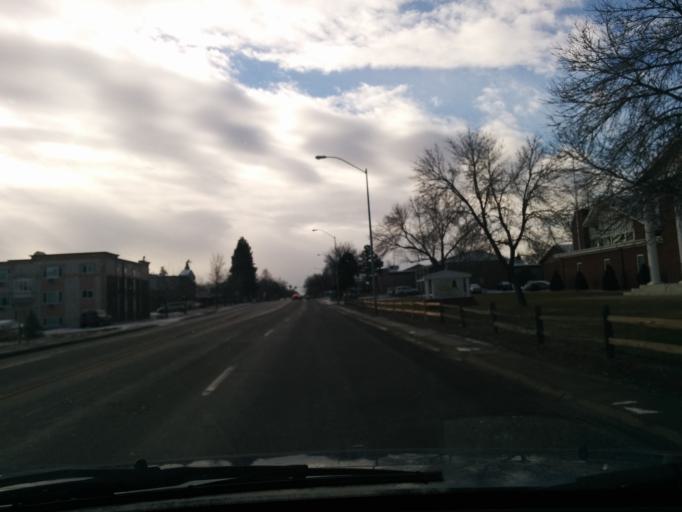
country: US
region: Colorado
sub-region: Larimer County
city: Fort Collins
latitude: 40.5770
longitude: -105.1151
